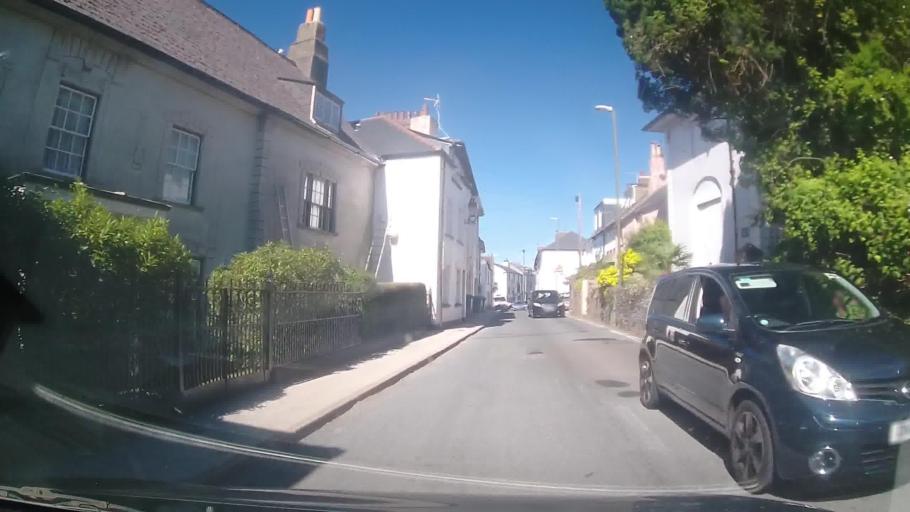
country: GB
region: England
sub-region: Borough of Torbay
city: Brixham
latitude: 50.3855
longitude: -3.5215
